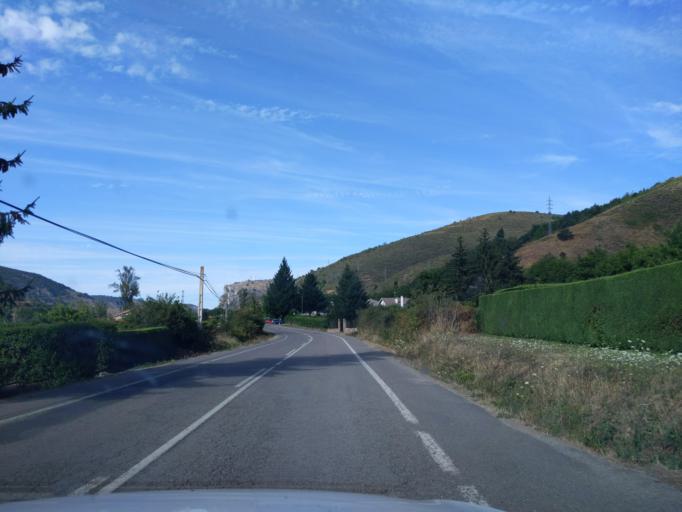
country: ES
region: La Rioja
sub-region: Provincia de La Rioja
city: Ezcaray
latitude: 42.3116
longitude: -3.0162
